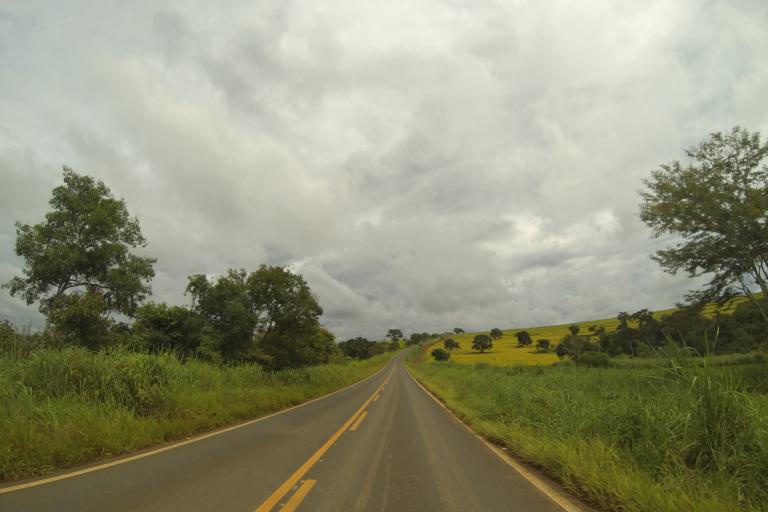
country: BR
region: Minas Gerais
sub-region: Bambui
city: Bambui
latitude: -20.1048
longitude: -46.1130
